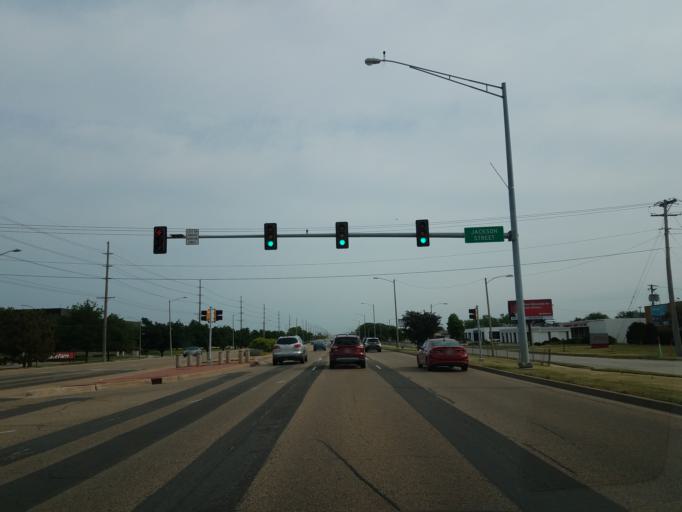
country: US
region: Illinois
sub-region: McLean County
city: Bloomington
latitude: 40.4753
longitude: -88.9525
